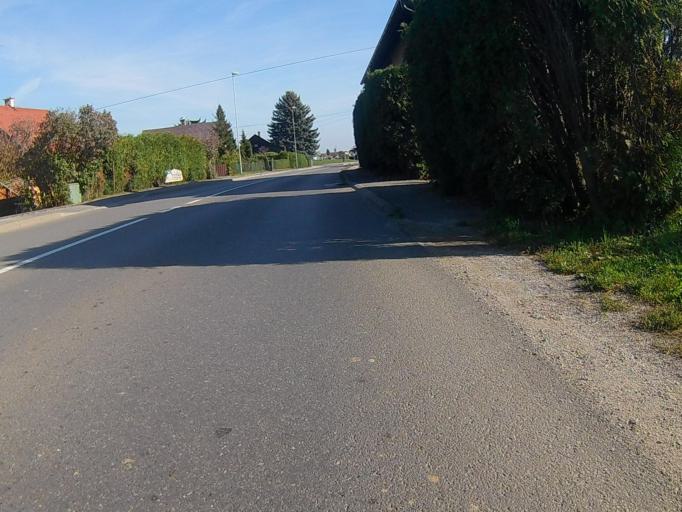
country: SI
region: Ptuj
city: Ptuj
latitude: 46.4271
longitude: 15.8888
